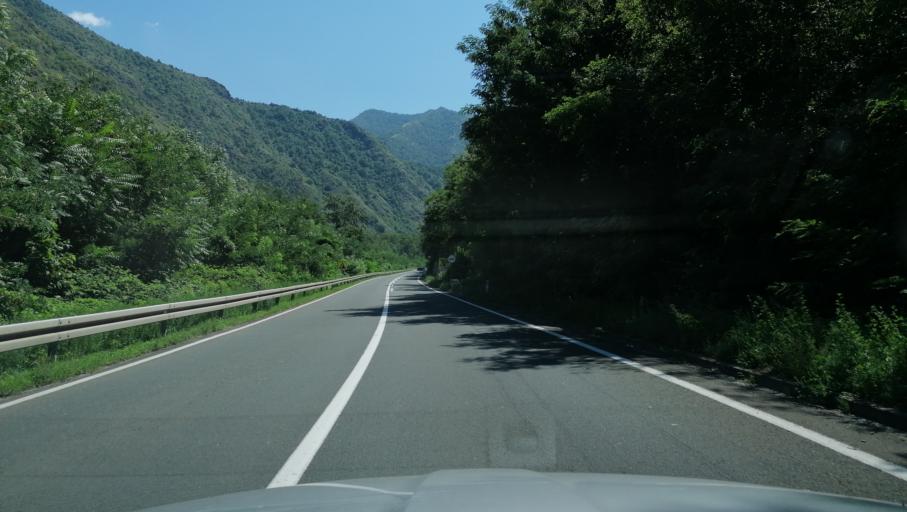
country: RS
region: Central Serbia
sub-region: Raski Okrug
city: Kraljevo
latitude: 43.6241
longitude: 20.5470
